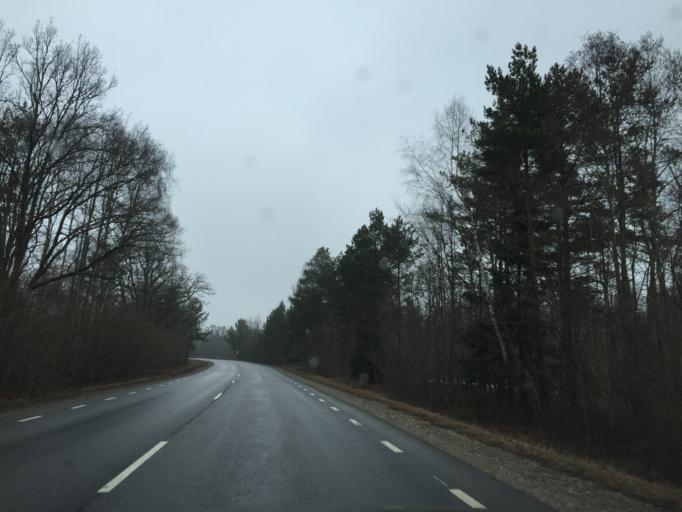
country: EE
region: Laeaene
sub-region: Lihula vald
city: Lihula
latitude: 58.6112
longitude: 23.6953
